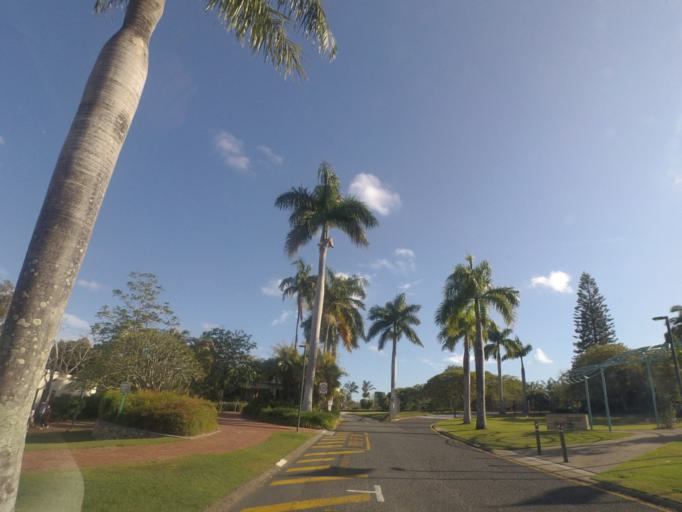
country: AU
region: Queensland
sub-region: Brisbane
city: Toowong
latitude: -27.4755
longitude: 152.9766
